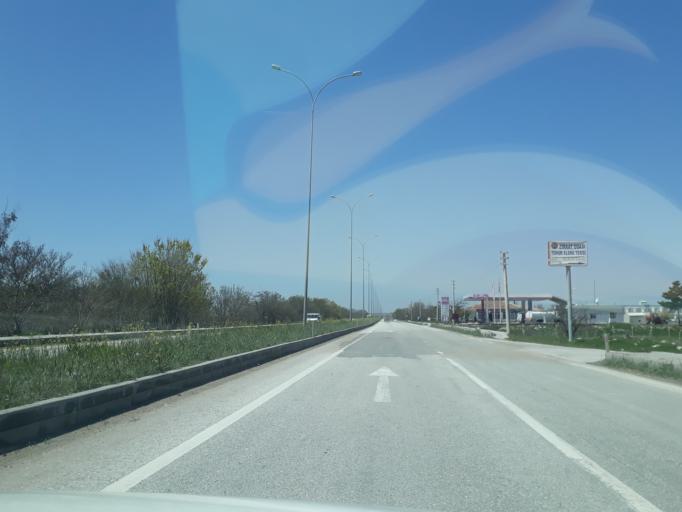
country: TR
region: Konya
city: Karapinar
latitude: 37.7140
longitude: 33.5266
